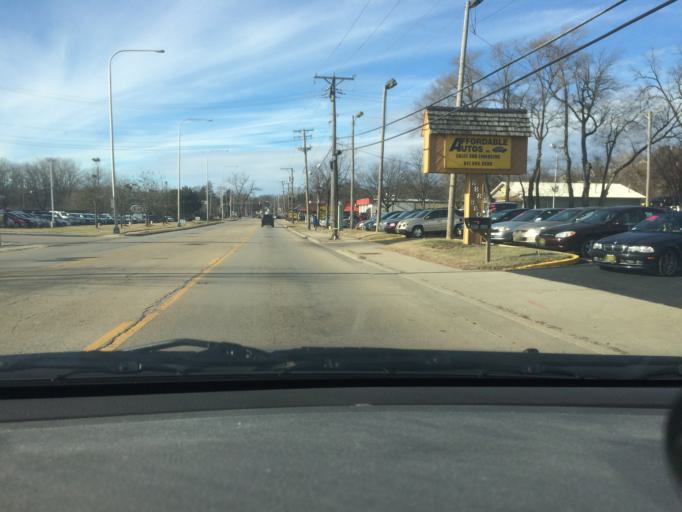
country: US
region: Illinois
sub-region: Kane County
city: Elgin
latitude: 42.0346
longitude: -88.2569
